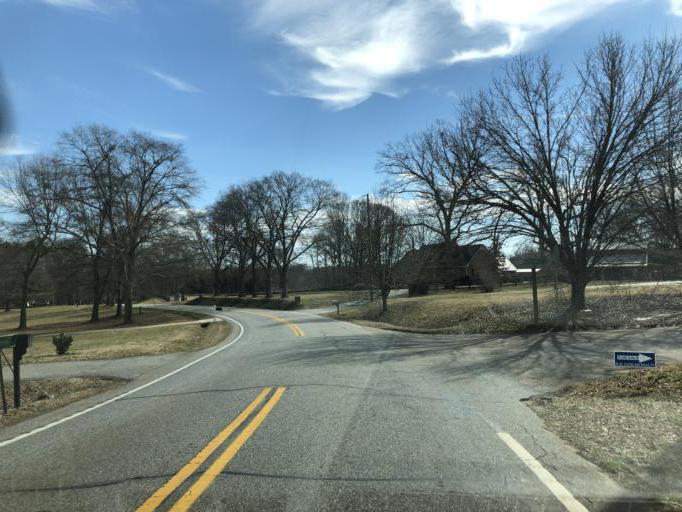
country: US
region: South Carolina
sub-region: Spartanburg County
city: Mayo
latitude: 35.0510
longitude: -81.8971
